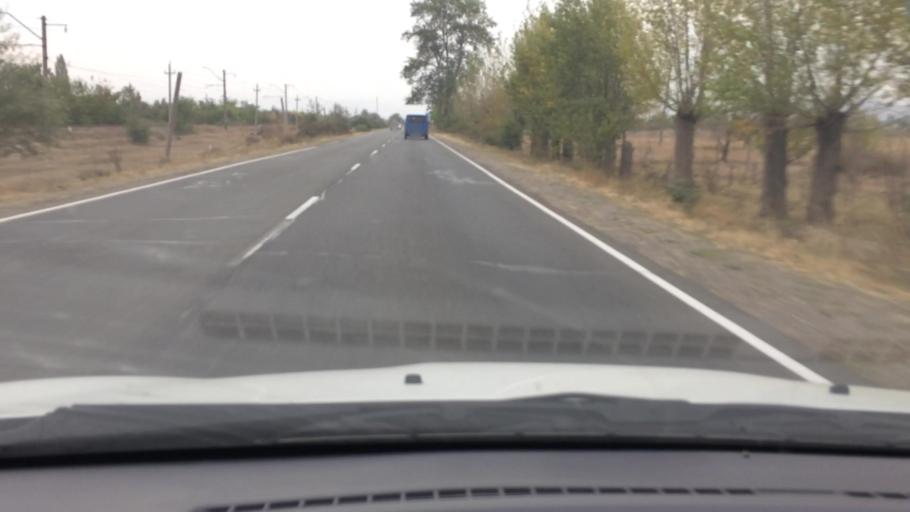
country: GE
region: Kvemo Kartli
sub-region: Marneuli
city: Marneuli
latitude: 41.4439
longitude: 44.8161
